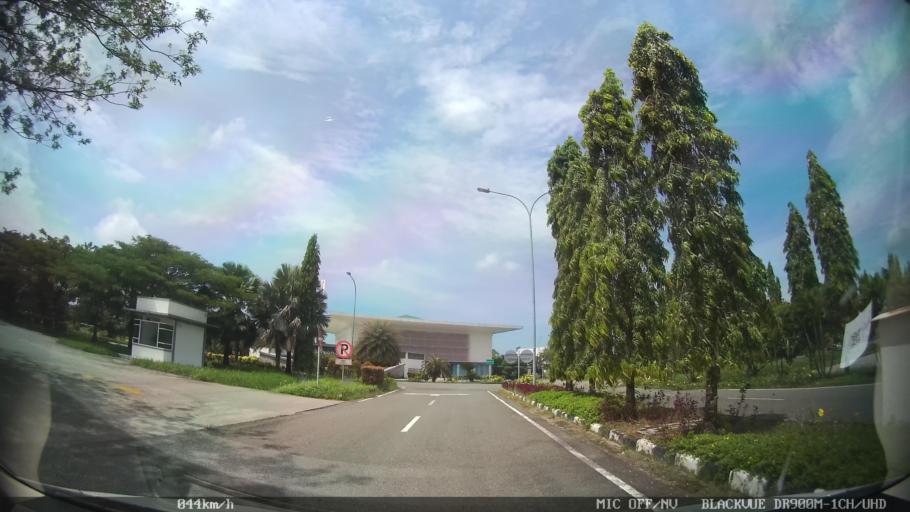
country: ID
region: North Sumatra
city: Percut
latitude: 3.6292
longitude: 98.8699
